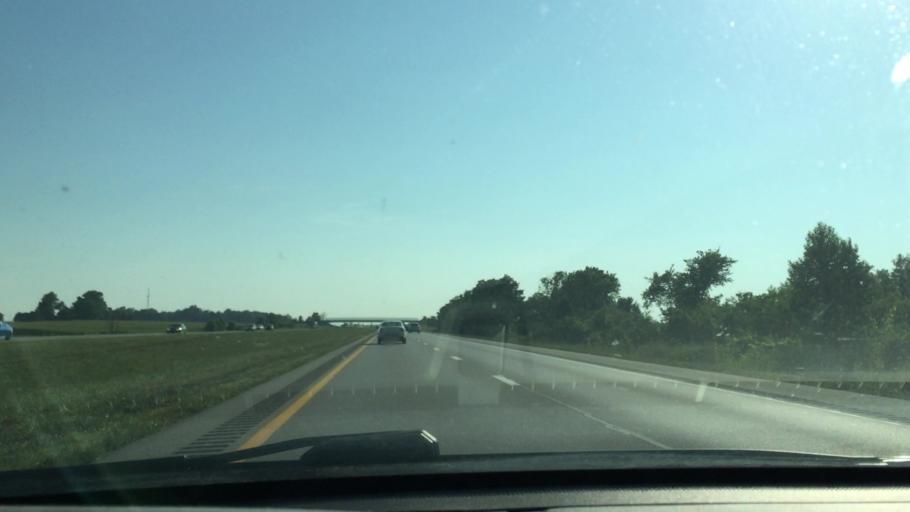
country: US
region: Ohio
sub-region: Clinton County
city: Wilmington
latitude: 39.4957
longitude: -83.9136
